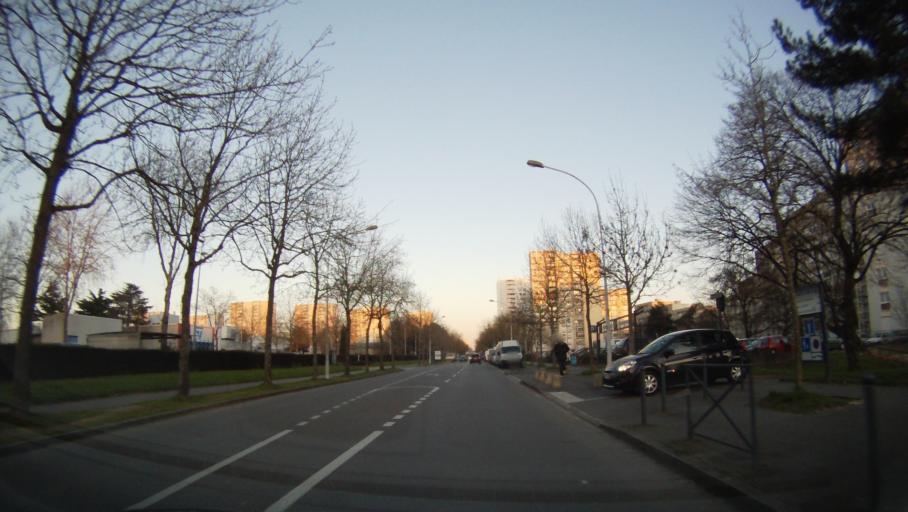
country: FR
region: Brittany
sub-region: Departement d'Ille-et-Vilaine
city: Rennes
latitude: 48.0865
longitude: -1.6670
